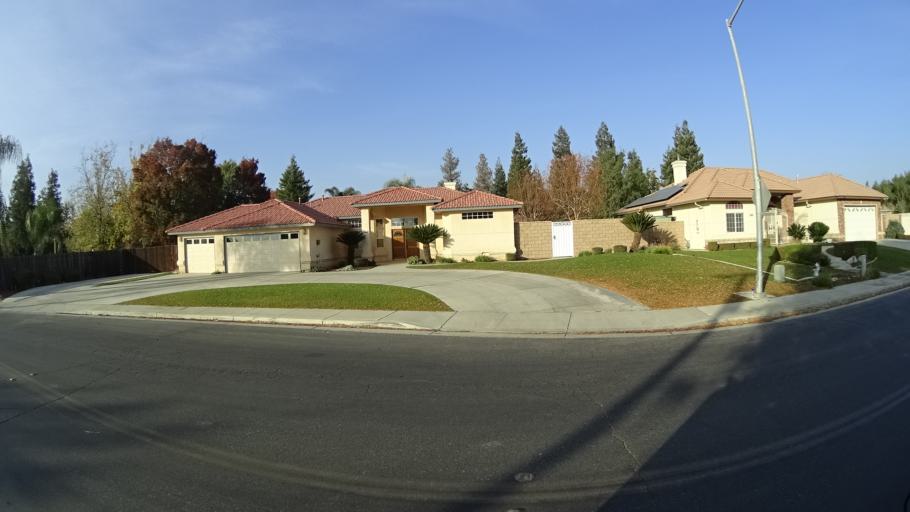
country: US
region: California
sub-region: Kern County
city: Greenacres
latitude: 35.3727
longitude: -119.1236
